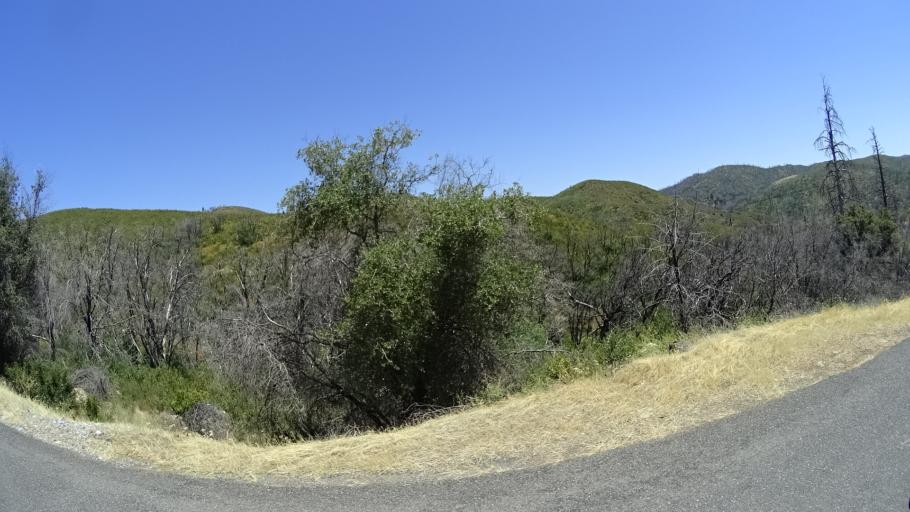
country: US
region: California
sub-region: Calaveras County
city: Mountain Ranch
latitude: 38.2872
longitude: -120.6228
